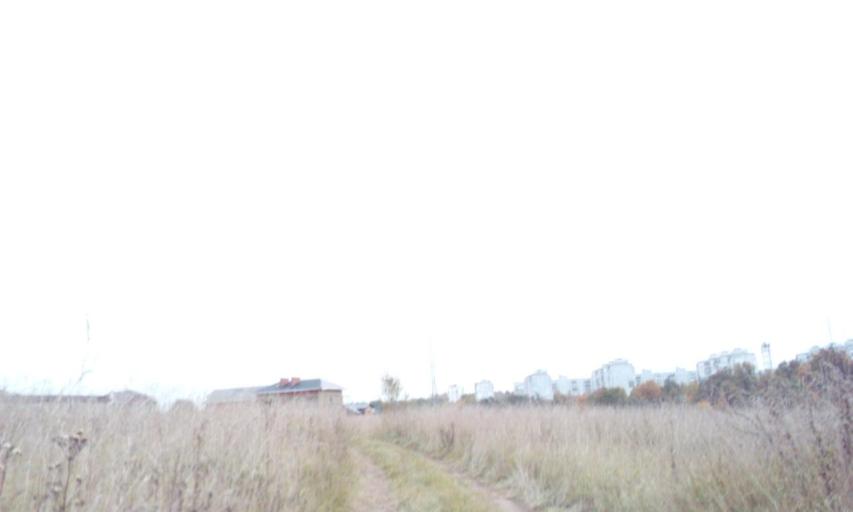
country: RU
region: Moskovskaya
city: Gorki Vtoryye
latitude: 55.6951
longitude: 37.2010
